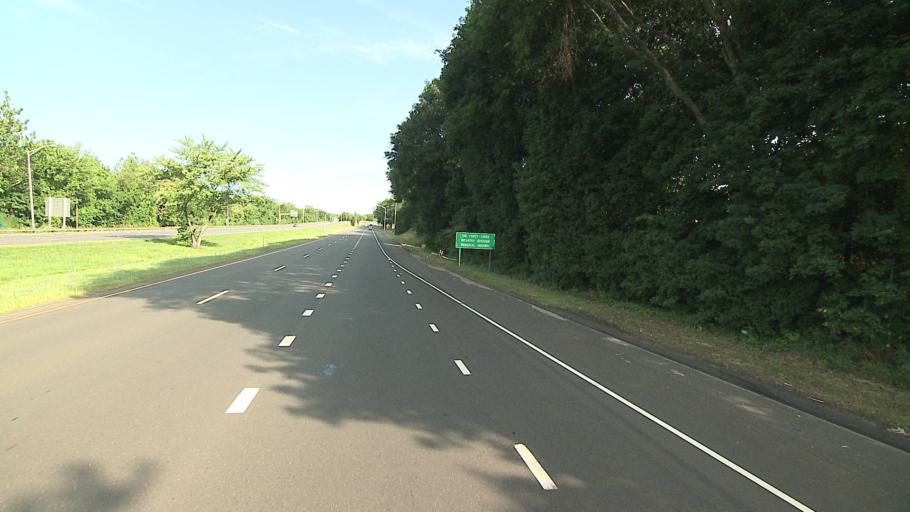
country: US
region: Connecticut
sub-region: Fairfield County
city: Norwalk
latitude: 41.1213
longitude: -73.4219
